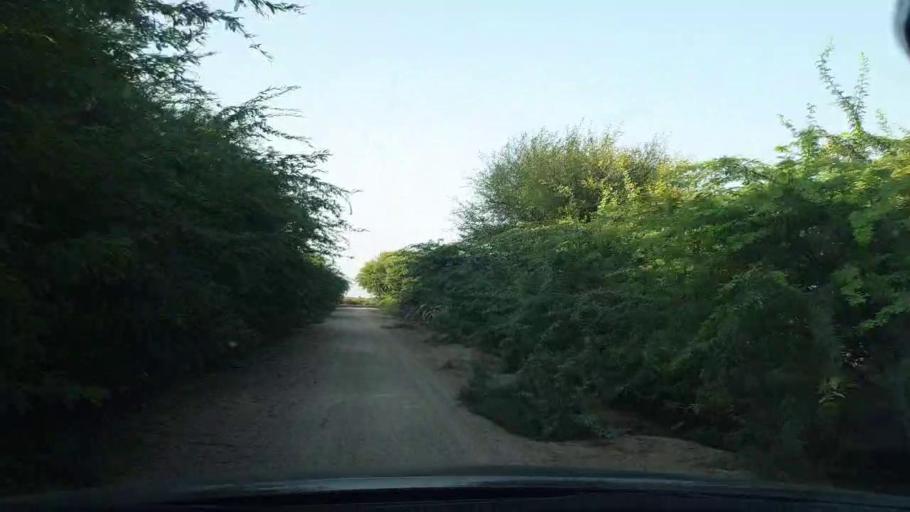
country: PK
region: Sindh
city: Naukot
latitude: 24.8138
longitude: 69.2043
